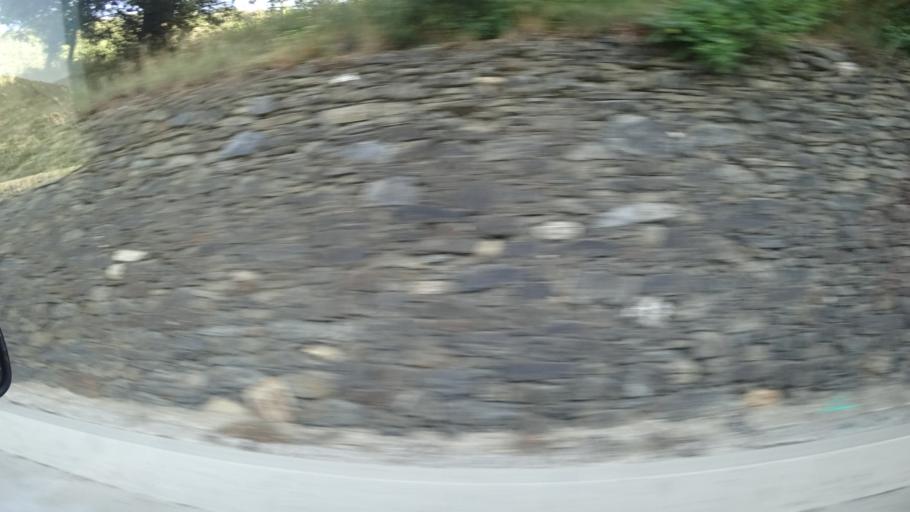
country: FR
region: Languedoc-Roussillon
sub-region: Departement des Pyrenees-Orientales
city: Vernet-les-Bains
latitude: 42.5613
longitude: 2.2965
